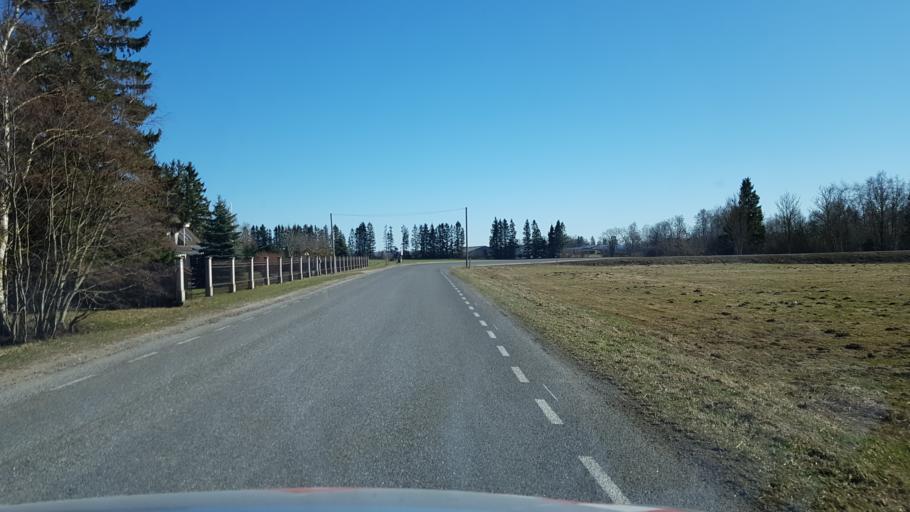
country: EE
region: Laeaene-Virumaa
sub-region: Someru vald
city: Someru
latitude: 59.3682
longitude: 26.4503
